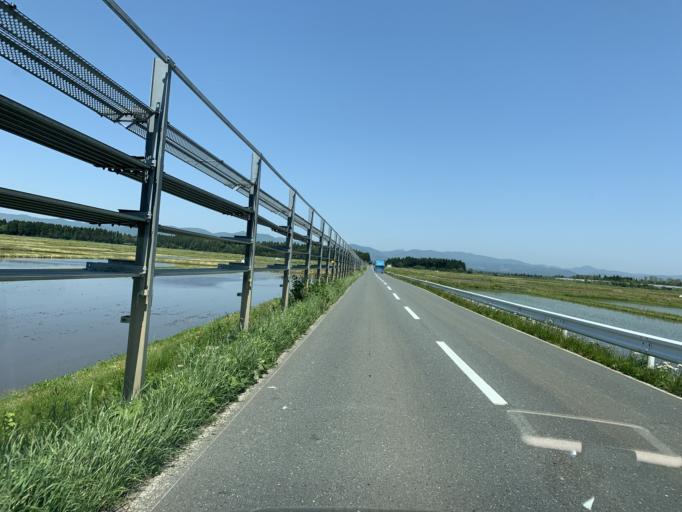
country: JP
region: Iwate
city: Kitakami
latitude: 39.2693
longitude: 141.0565
